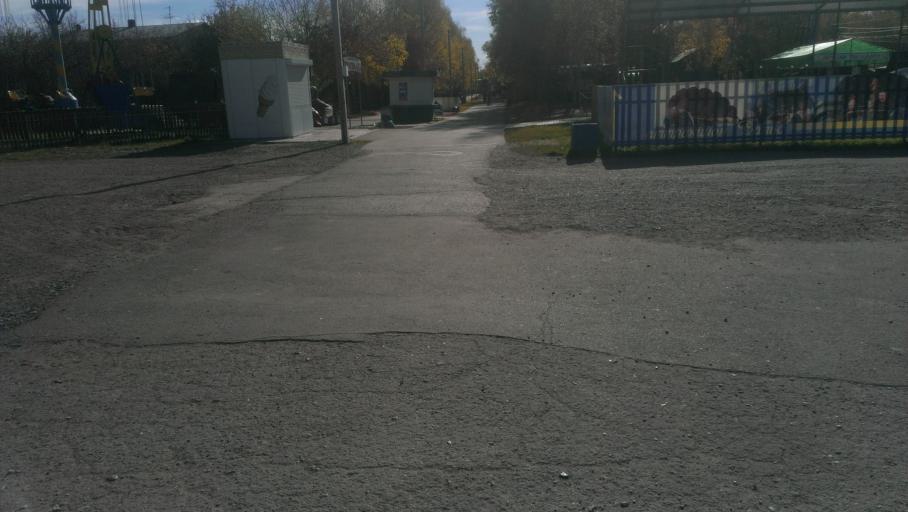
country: RU
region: Altai Krai
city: Novosilikatnyy
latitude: 53.3580
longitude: 83.6848
